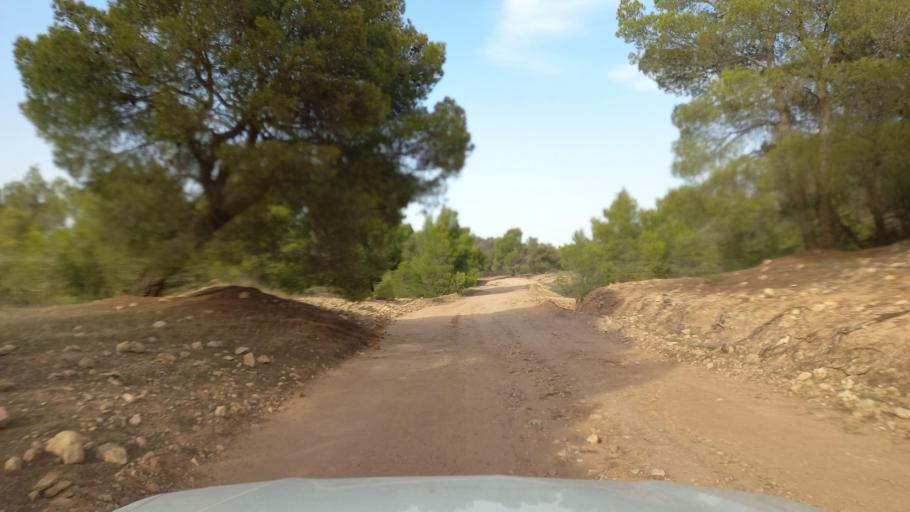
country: TN
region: Al Qasrayn
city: Kasserine
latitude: 35.3415
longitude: 8.8595
